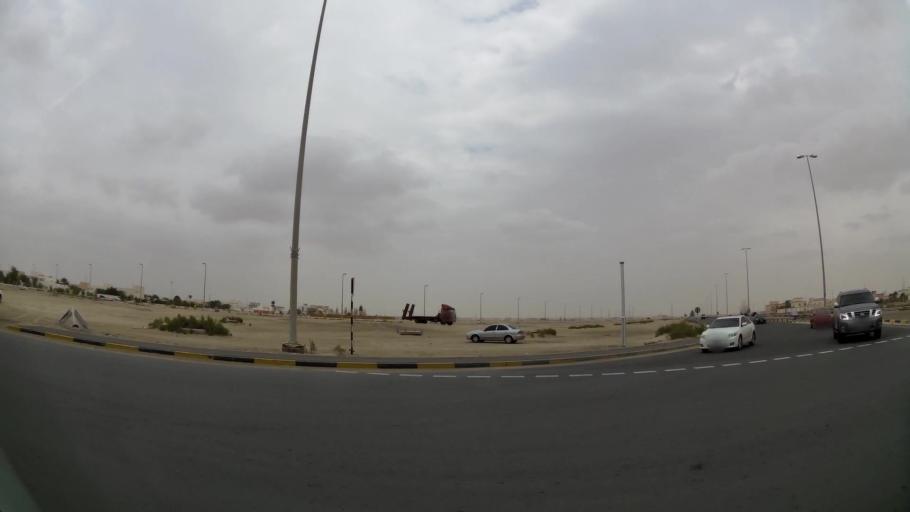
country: AE
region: Abu Dhabi
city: Abu Dhabi
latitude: 24.3648
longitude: 54.6609
